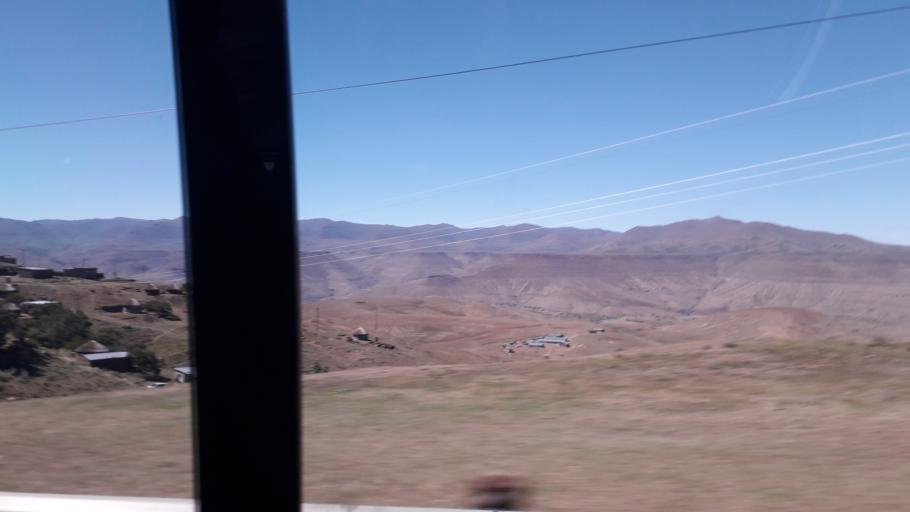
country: LS
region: Mokhotlong
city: Mokhotlong
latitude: -29.2806
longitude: 28.9439
